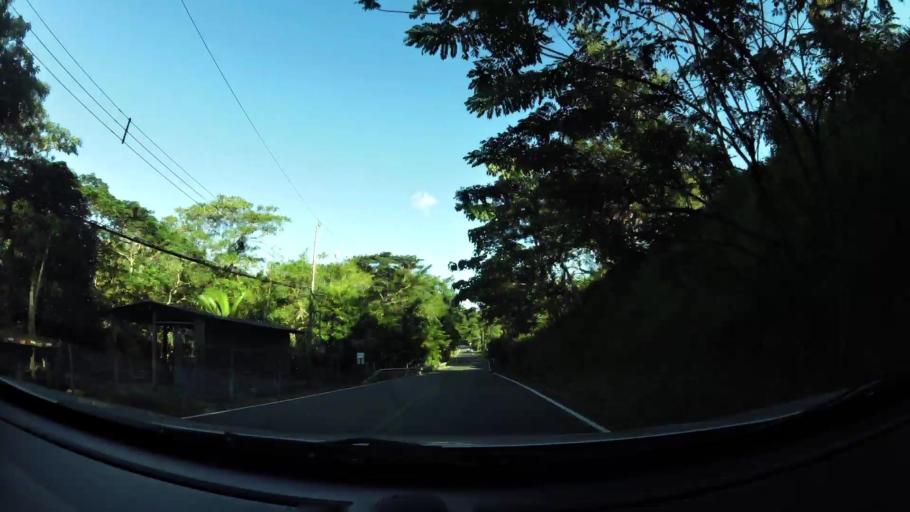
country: CR
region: Guanacaste
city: Juntas
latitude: 10.2006
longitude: -84.8447
